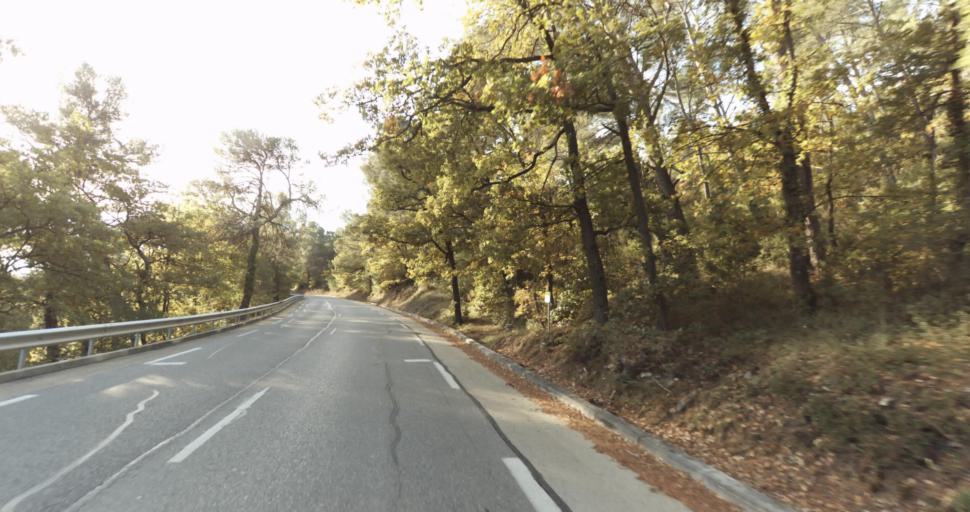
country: FR
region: Provence-Alpes-Cote d'Azur
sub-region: Departement des Bouches-du-Rhone
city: Venelles
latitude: 43.6184
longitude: 5.4625
